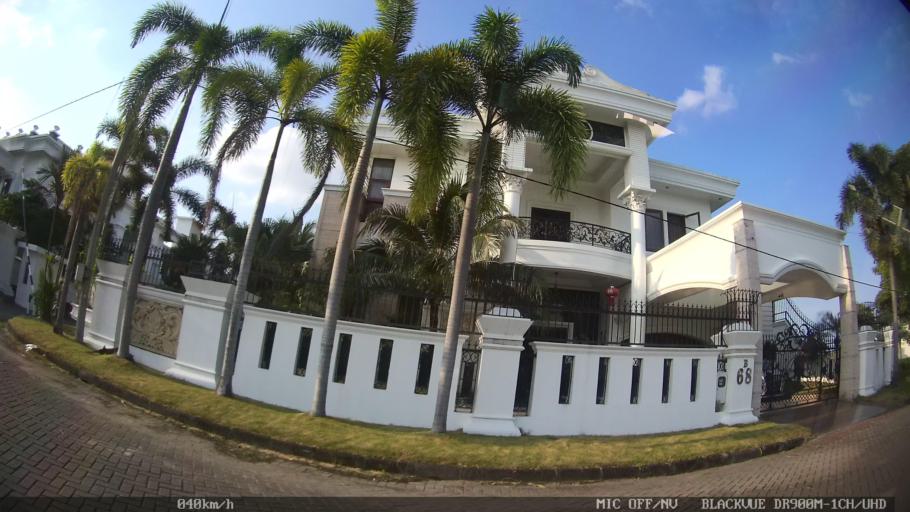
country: ID
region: North Sumatra
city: Medan
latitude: 3.6253
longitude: 98.6488
